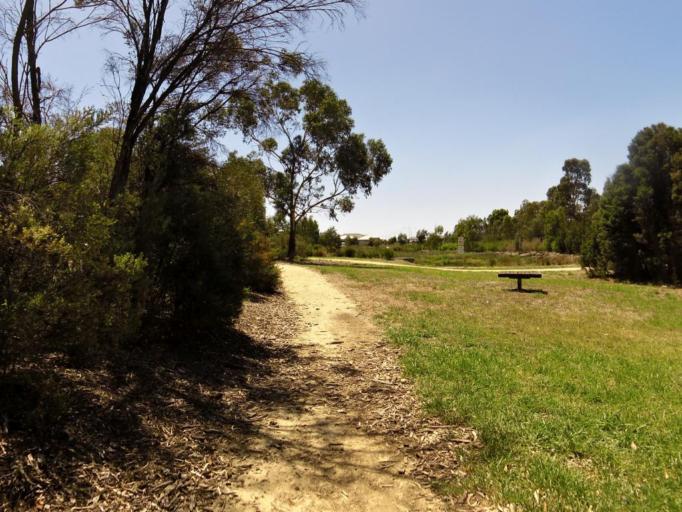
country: AU
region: Victoria
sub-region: Whittlesea
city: Lalor
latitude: -37.6683
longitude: 144.9854
